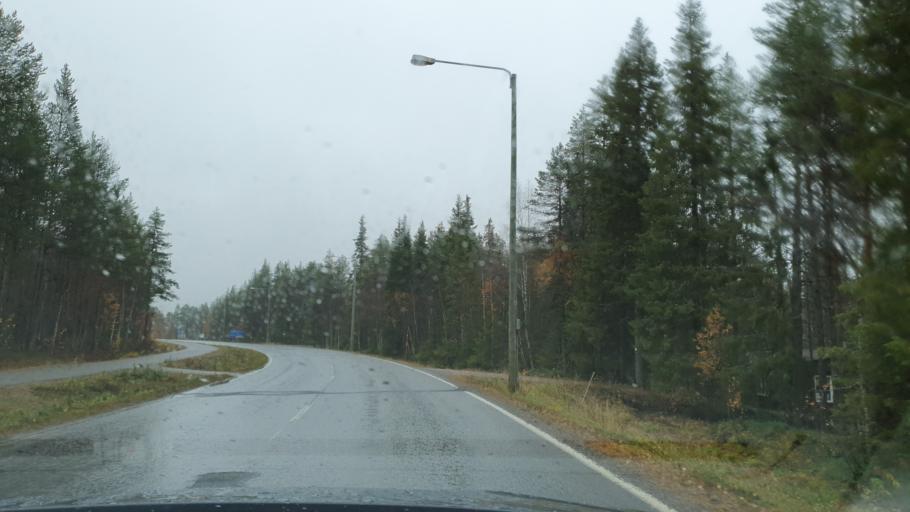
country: FI
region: Lapland
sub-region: Tunturi-Lappi
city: Kolari
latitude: 67.6030
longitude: 24.1358
